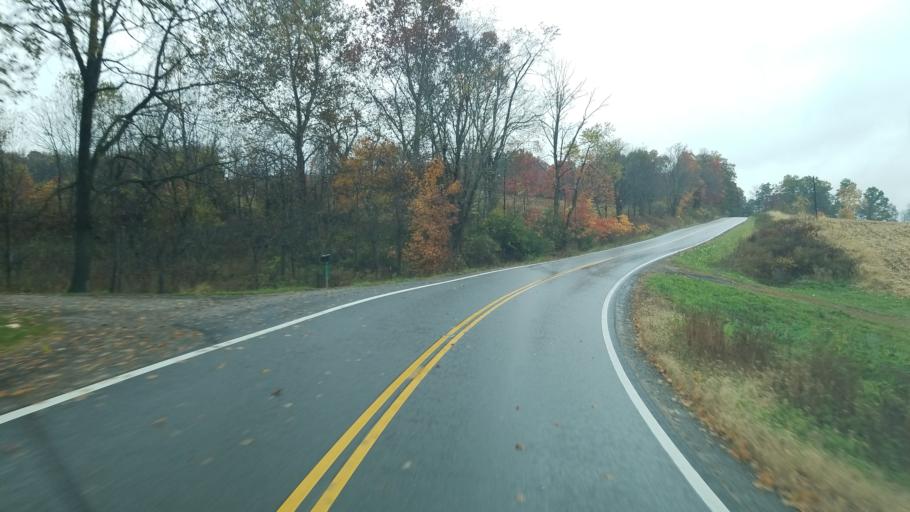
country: US
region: Ohio
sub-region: Coshocton County
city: Coshocton
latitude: 40.3506
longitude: -81.8539
